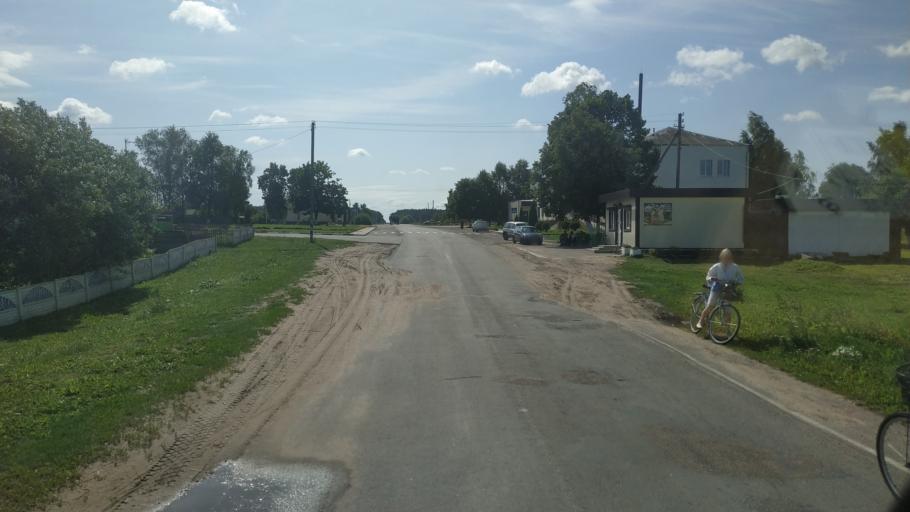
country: BY
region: Mogilev
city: Ramanavichy
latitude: 53.7044
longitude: 30.5053
